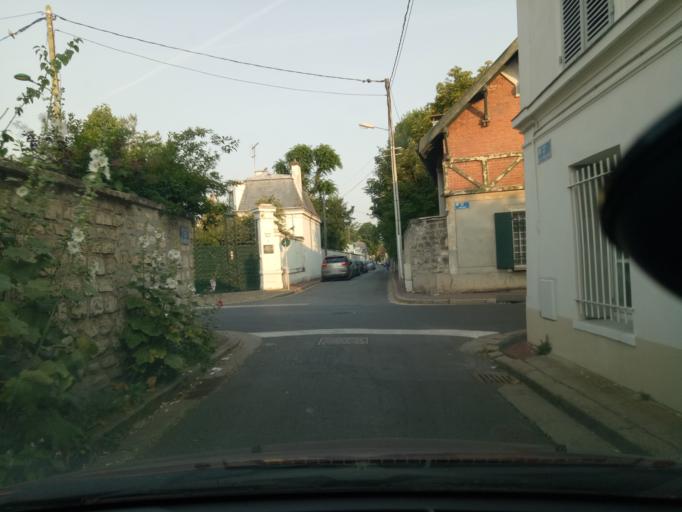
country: FR
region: Ile-de-France
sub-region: Departement des Yvelines
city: Chatou
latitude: 48.8819
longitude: 2.1518
